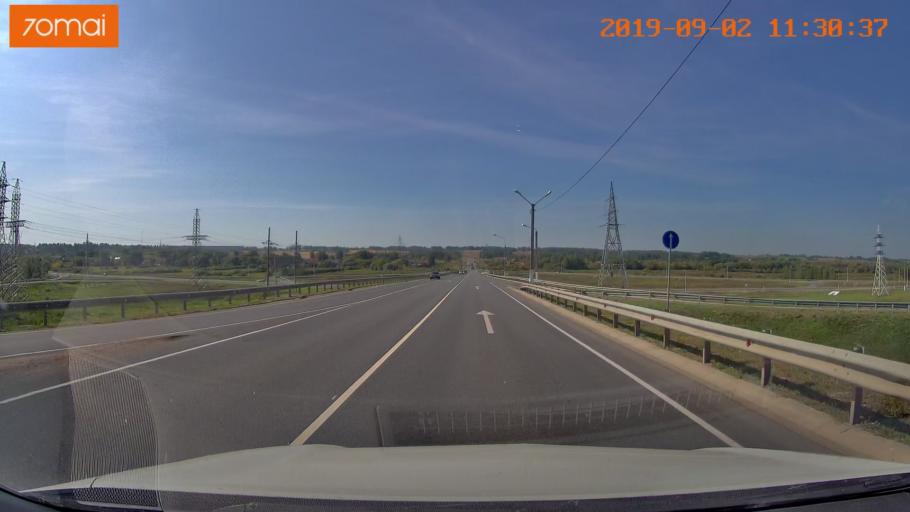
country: RU
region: Smolensk
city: Oster
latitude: 53.9824
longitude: 32.8303
